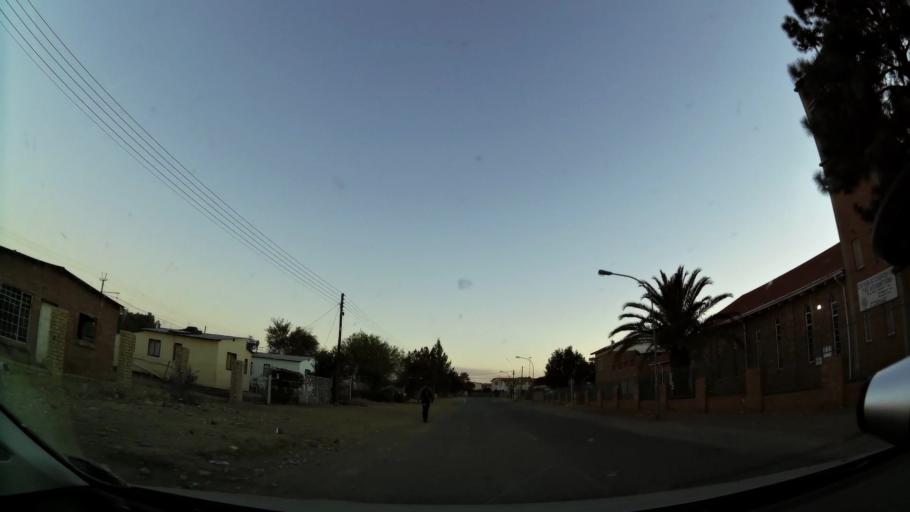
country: ZA
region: Northern Cape
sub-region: Frances Baard District Municipality
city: Kimberley
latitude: -28.7149
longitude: 24.7684
